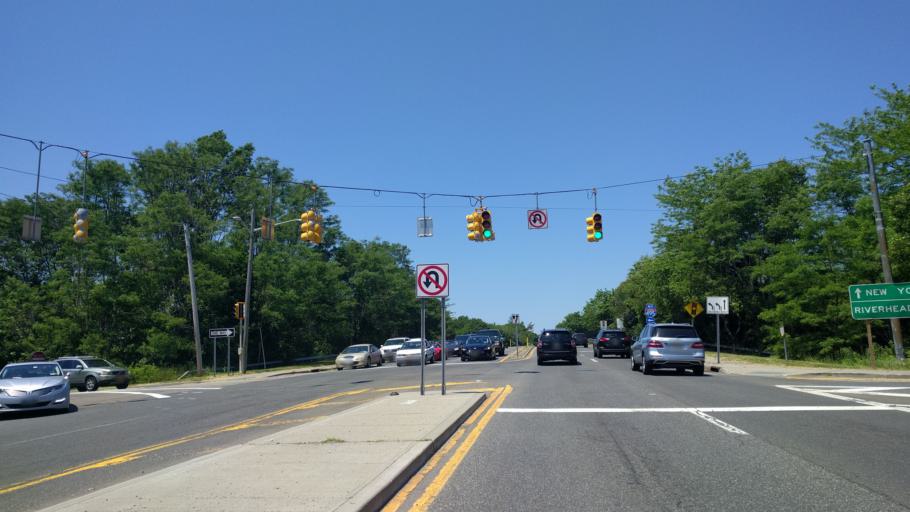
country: US
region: New York
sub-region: Suffolk County
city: Manorville
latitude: 40.8711
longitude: -72.8002
